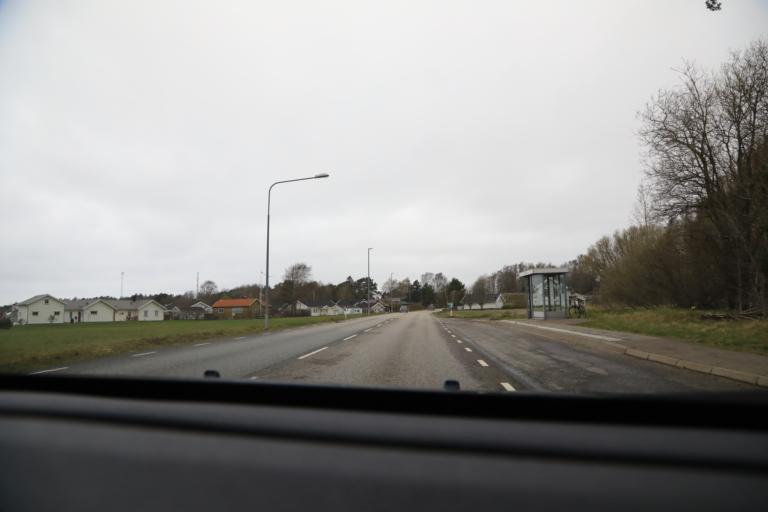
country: SE
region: Halland
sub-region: Kungsbacka Kommun
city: Frillesas
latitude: 57.3128
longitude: 12.1800
